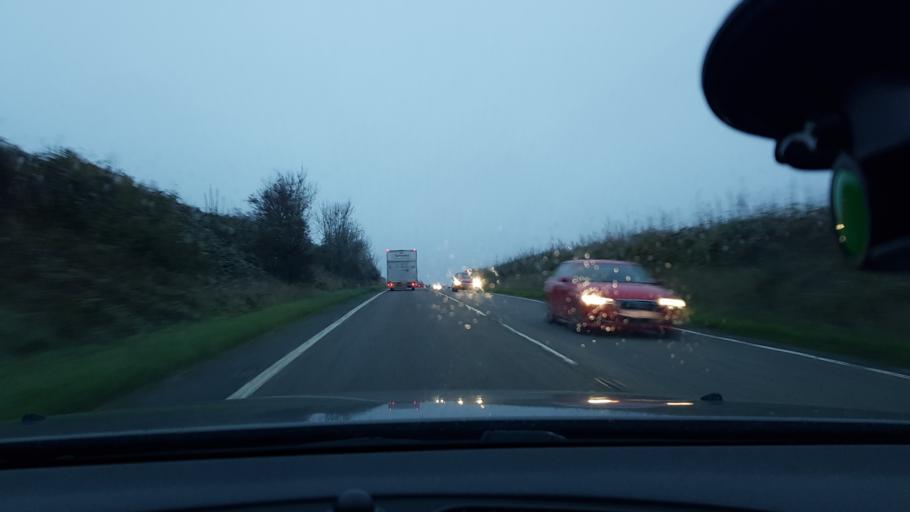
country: GB
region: England
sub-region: Dorset
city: Blandford Forum
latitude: 50.8418
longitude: -2.1769
